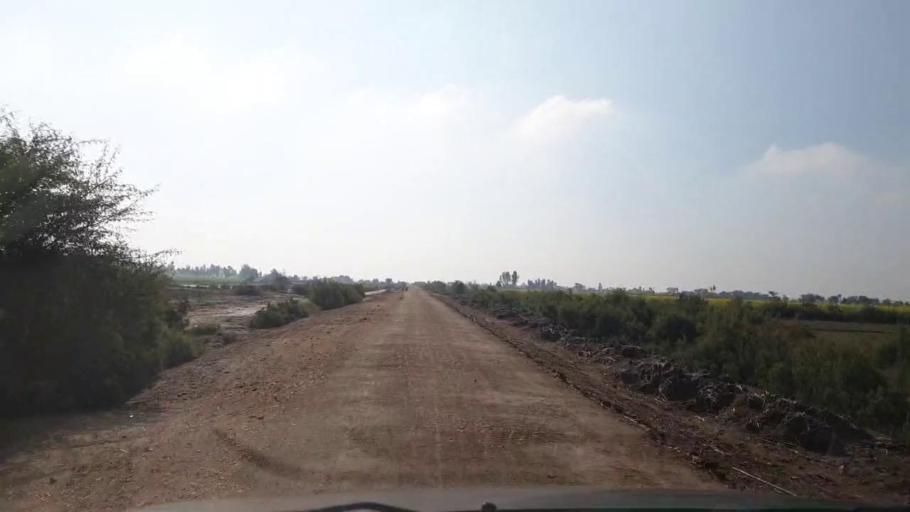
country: PK
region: Sindh
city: Sinjhoro
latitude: 26.0477
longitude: 68.7782
